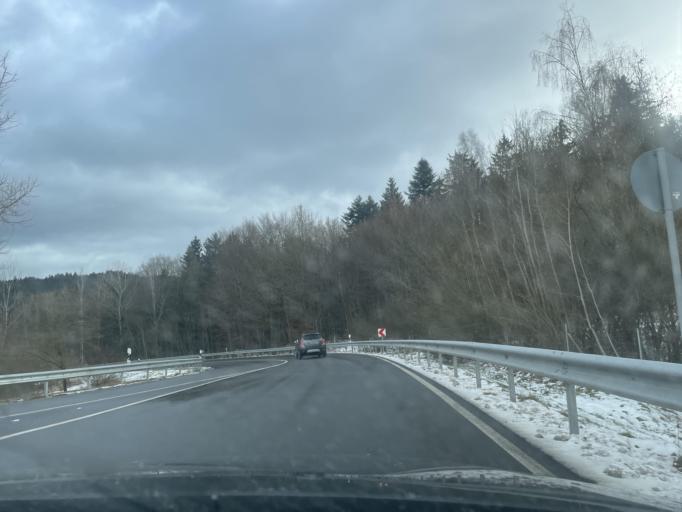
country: DE
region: Bavaria
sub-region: Upper Palatinate
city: Arnschwang
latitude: 49.2907
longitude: 12.8246
